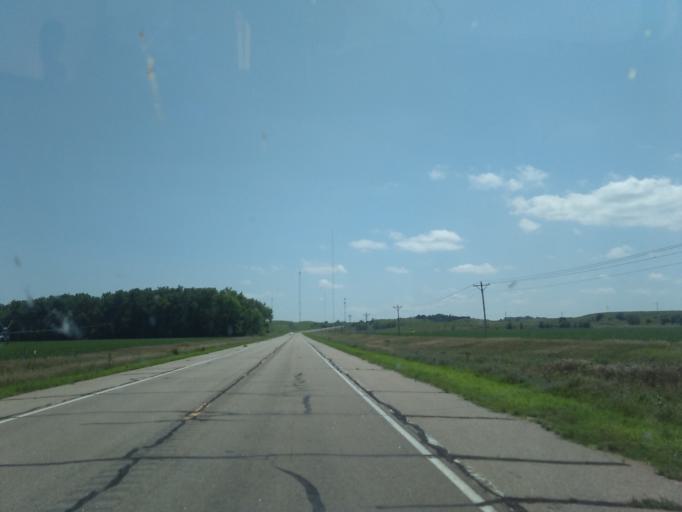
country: US
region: Nebraska
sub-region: Dawson County
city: Lexington
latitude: 40.7139
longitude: -99.7874
